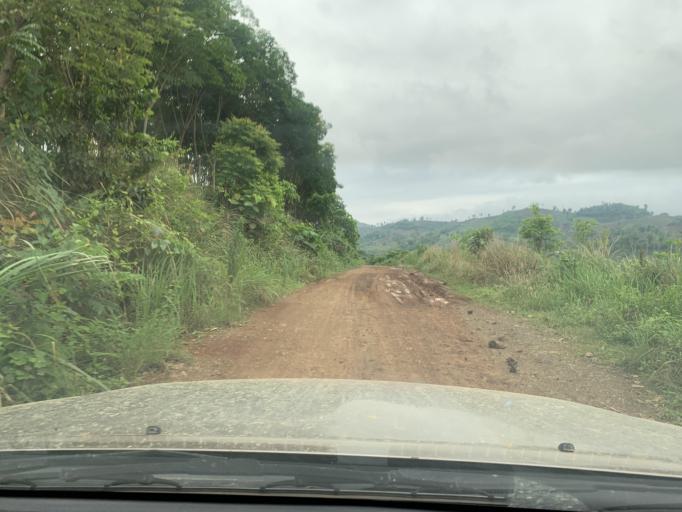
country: TH
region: Nan
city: Mae Charim
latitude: 18.4030
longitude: 101.4347
